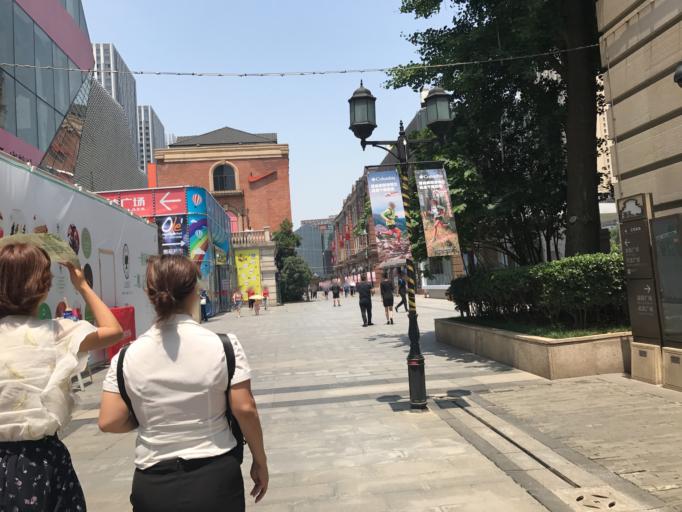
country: CN
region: Hubei
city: Jiang'an
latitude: 30.5596
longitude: 114.3345
